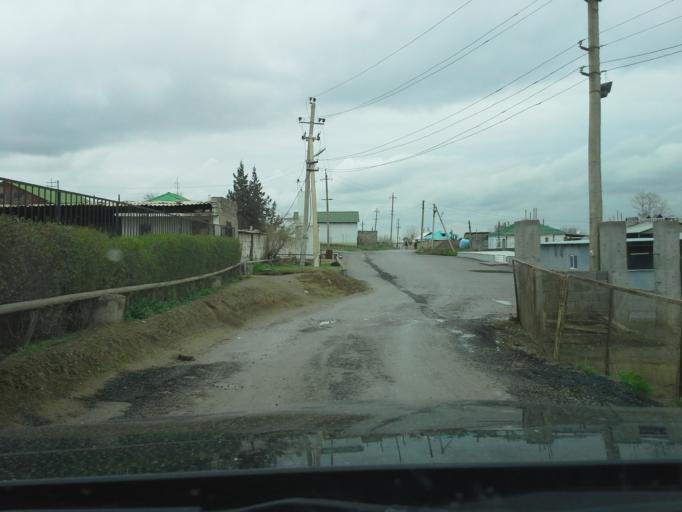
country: TM
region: Ahal
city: Abadan
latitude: 37.9608
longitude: 58.2217
